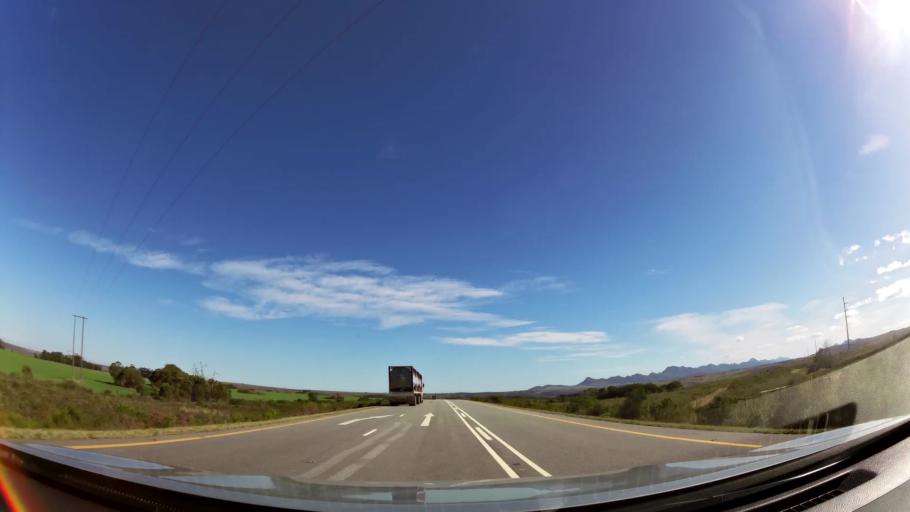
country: ZA
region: Eastern Cape
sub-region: Cacadu District Municipality
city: Kruisfontein
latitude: -34.0207
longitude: 24.6170
